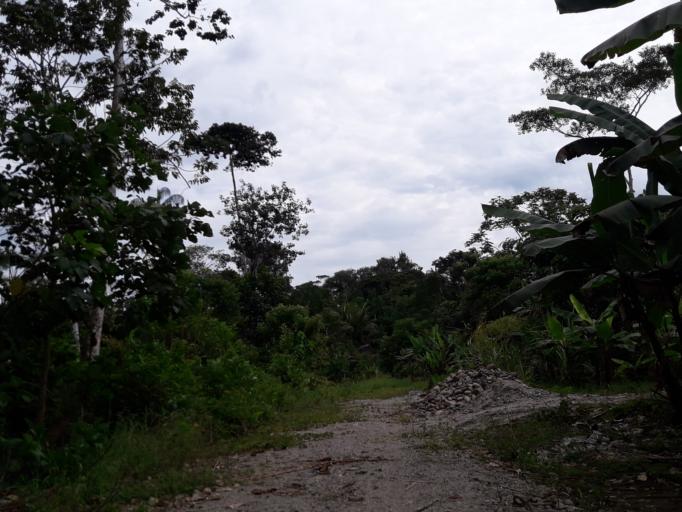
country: EC
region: Napo
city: Tena
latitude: -1.0550
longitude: -77.7934
